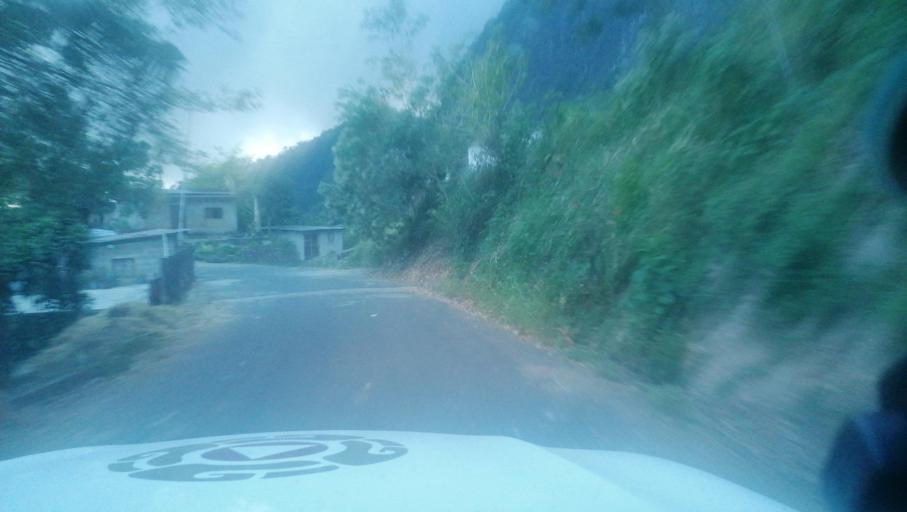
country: MX
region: Chiapas
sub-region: Cacahoatan
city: Benito Juarez
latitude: 15.1162
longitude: -92.2102
